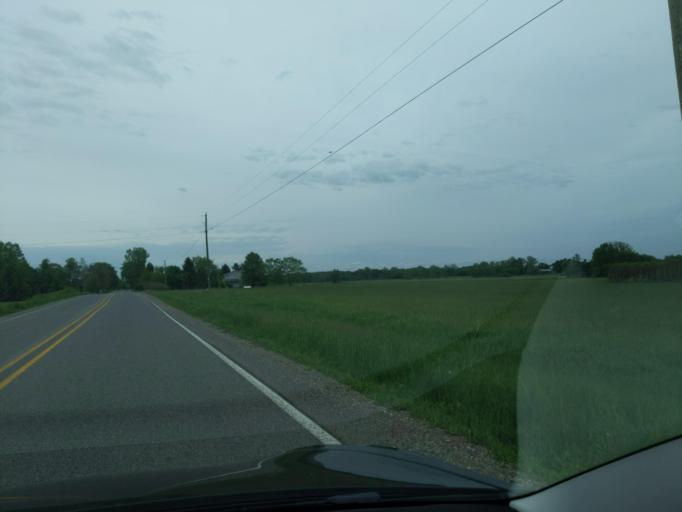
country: US
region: Michigan
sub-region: Ingham County
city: Leslie
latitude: 42.4928
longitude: -84.4265
